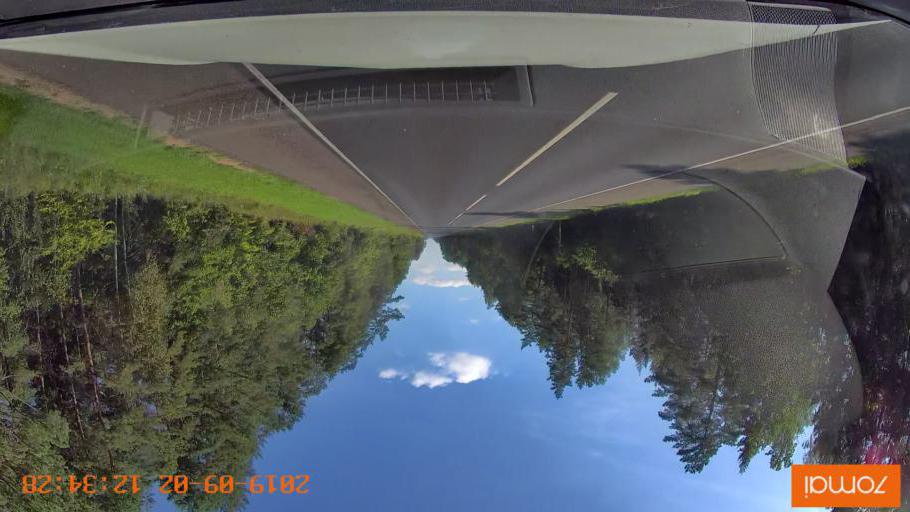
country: RU
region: Smolensk
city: Shumyachi
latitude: 53.8101
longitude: 32.4036
